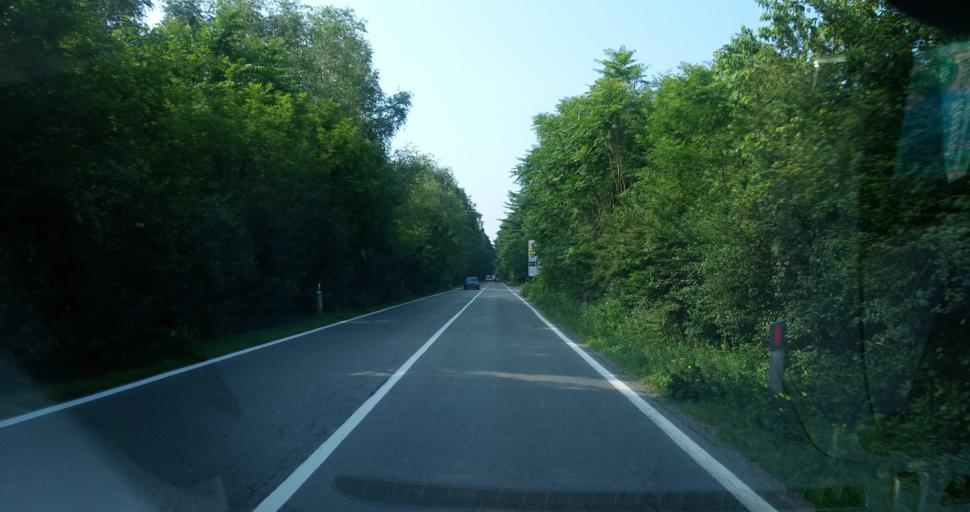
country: IT
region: Lombardy
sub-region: Provincia di Varese
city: Somma Lombardo
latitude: 45.6584
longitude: 8.7044
